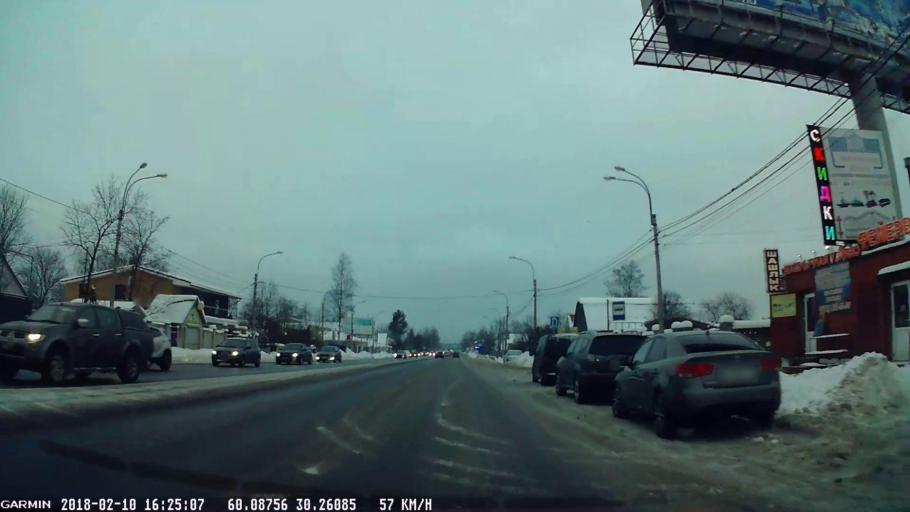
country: RU
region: St.-Petersburg
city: Pargolovo
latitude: 60.0885
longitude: 30.2602
